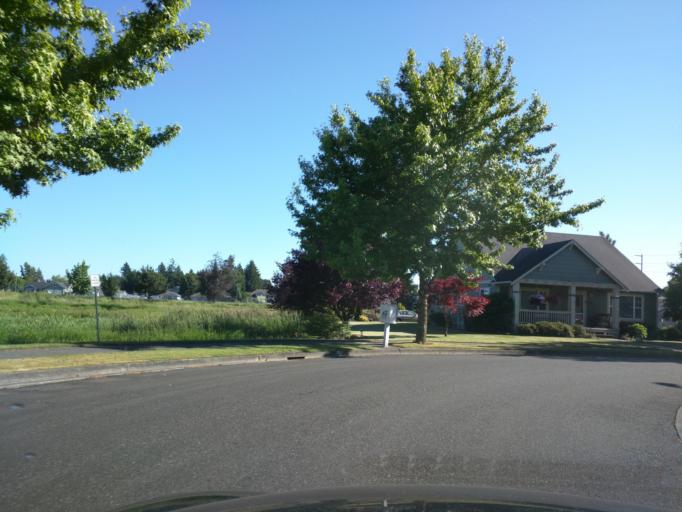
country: US
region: Washington
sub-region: Whatcom County
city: Lynden
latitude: 48.9608
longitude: -122.4284
